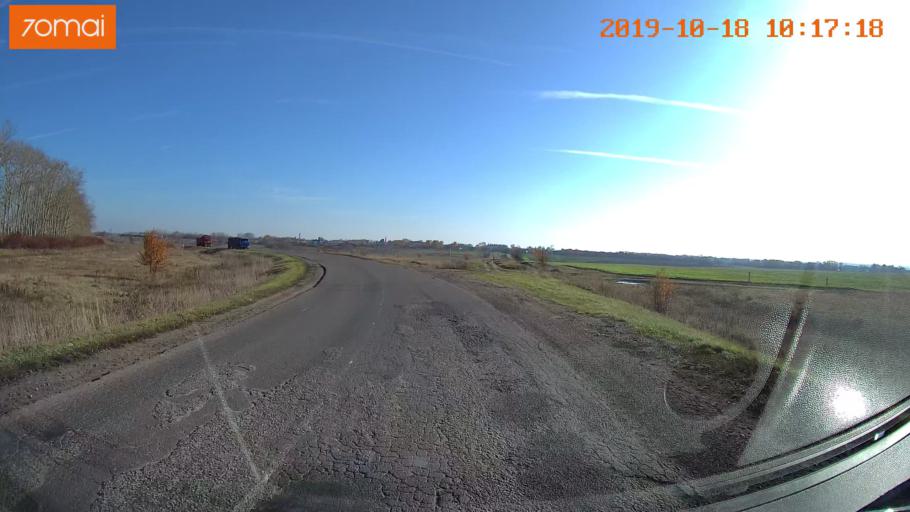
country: RU
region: Tula
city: Kurkino
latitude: 53.4114
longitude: 38.6160
